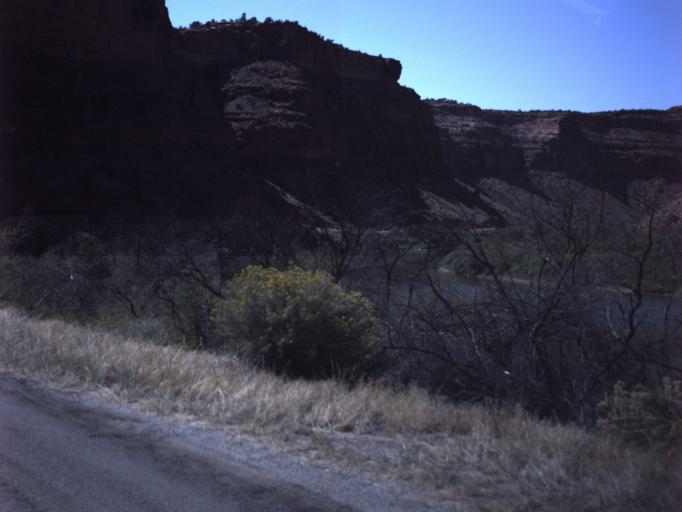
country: US
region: Utah
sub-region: Grand County
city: Moab
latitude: 38.7999
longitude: -109.3121
